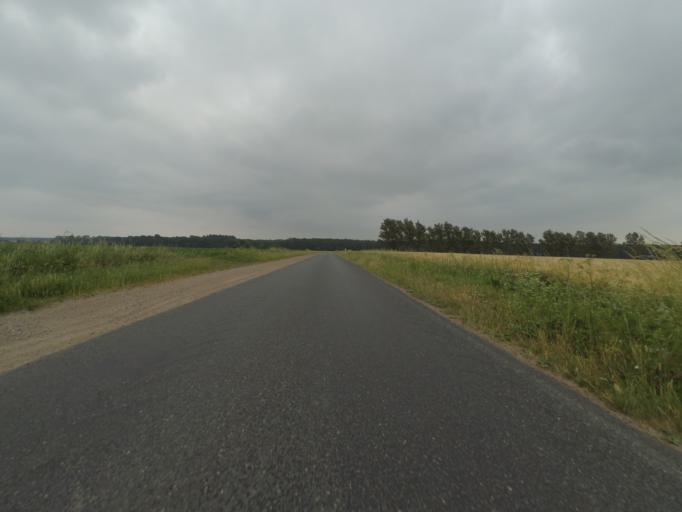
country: DE
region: Mecklenburg-Vorpommern
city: Spornitz
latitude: 53.3622
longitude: 11.6880
